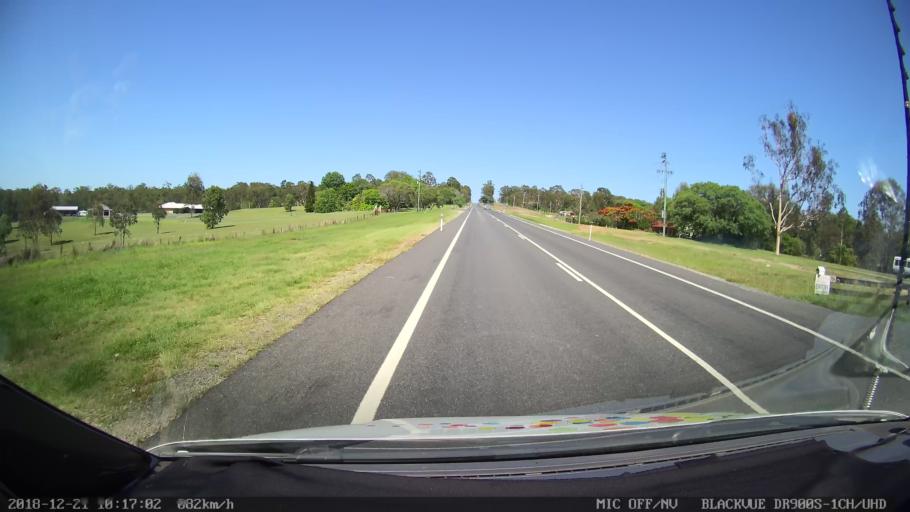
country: AU
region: New South Wales
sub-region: Clarence Valley
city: South Grafton
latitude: -29.6829
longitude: 152.8763
